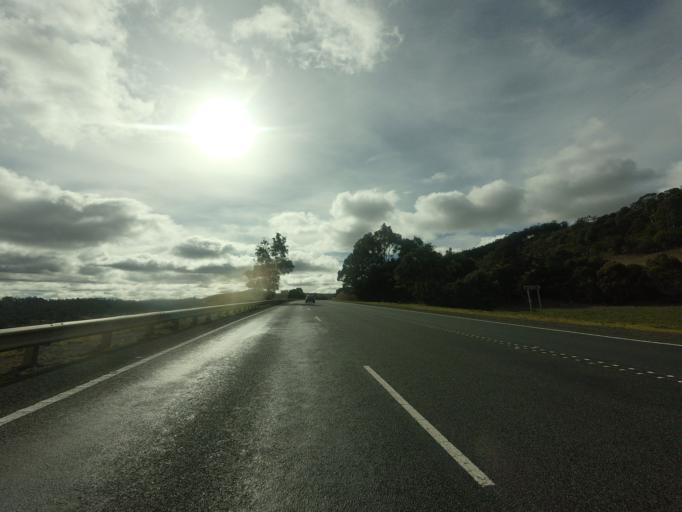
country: AU
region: Tasmania
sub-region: Brighton
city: Bridgewater
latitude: -42.4286
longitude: 147.2588
